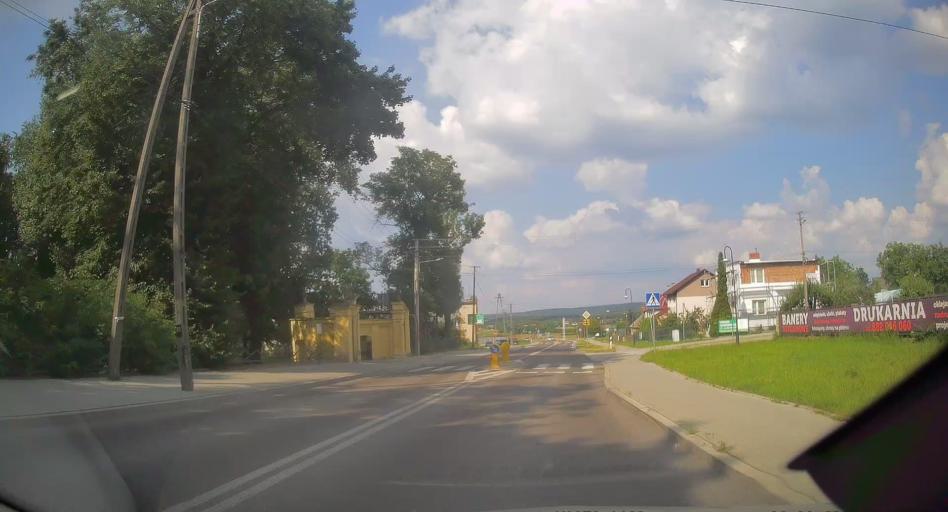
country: PL
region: Swietokrzyskie
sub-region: Powiat kielecki
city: Lopuszno
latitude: 50.9500
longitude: 20.2507
